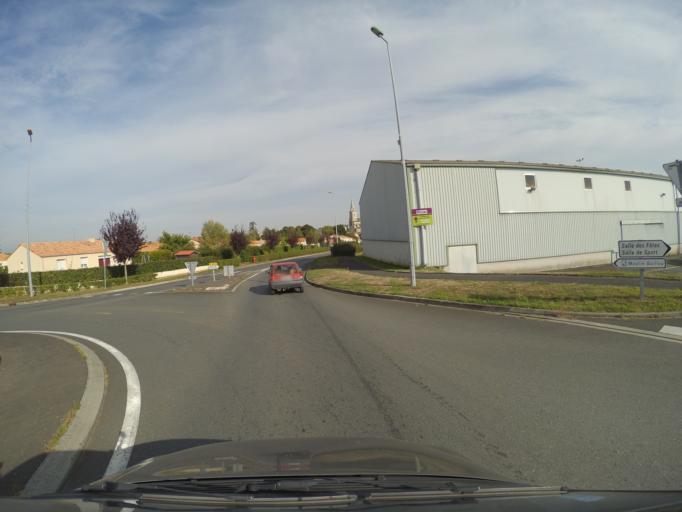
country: FR
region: Pays de la Loire
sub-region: Departement de Maine-et-Loire
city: Tillieres
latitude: 47.1412
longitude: -1.1649
